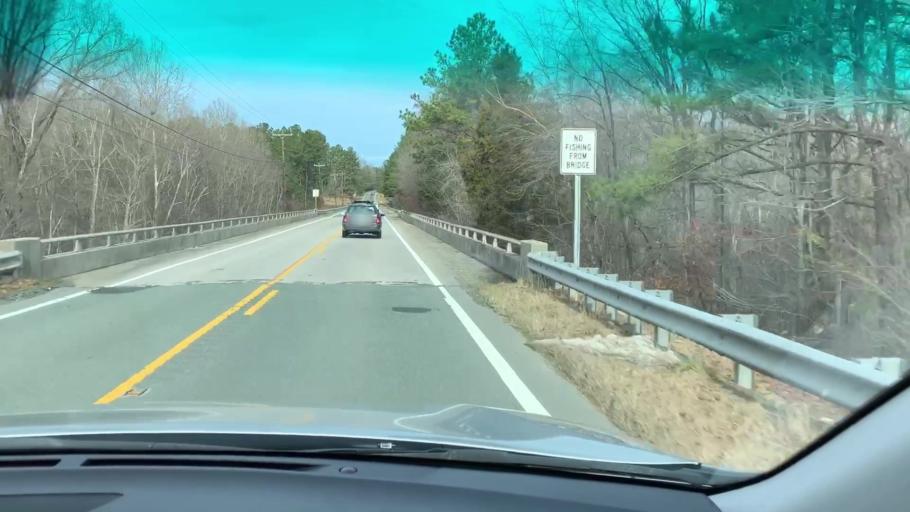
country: US
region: North Carolina
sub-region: Wake County
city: Green Level
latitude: 35.8551
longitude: -78.9396
